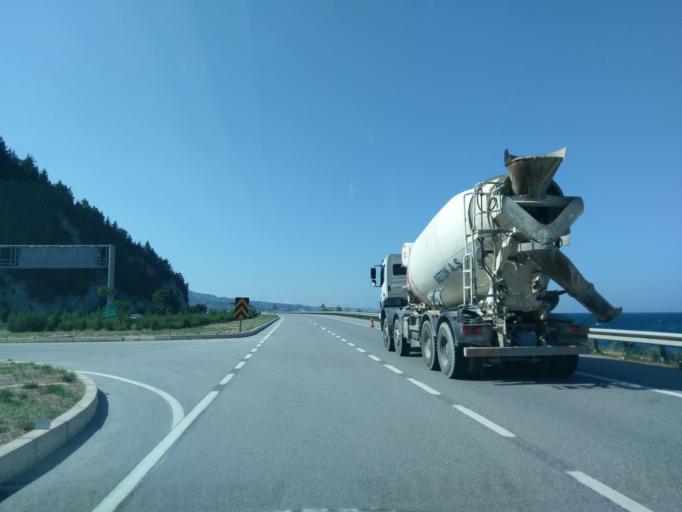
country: TR
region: Sinop
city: Gerze
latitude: 41.7487
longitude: 35.2415
